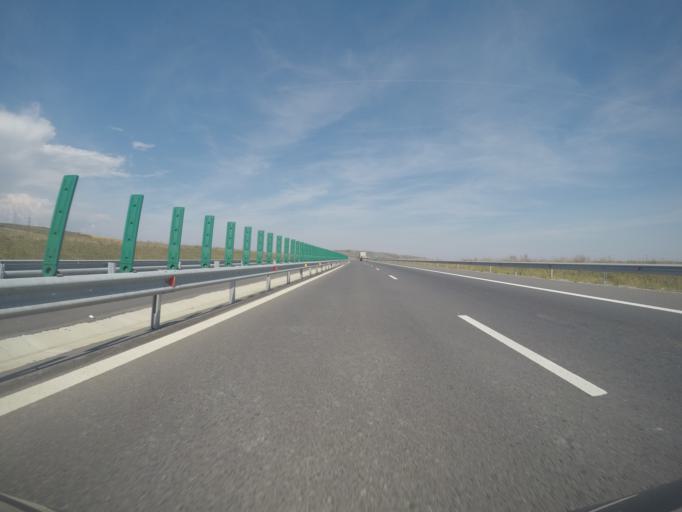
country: RO
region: Alba
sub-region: Comuna Unirea
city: Unirea
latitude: 46.3992
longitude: 23.7935
